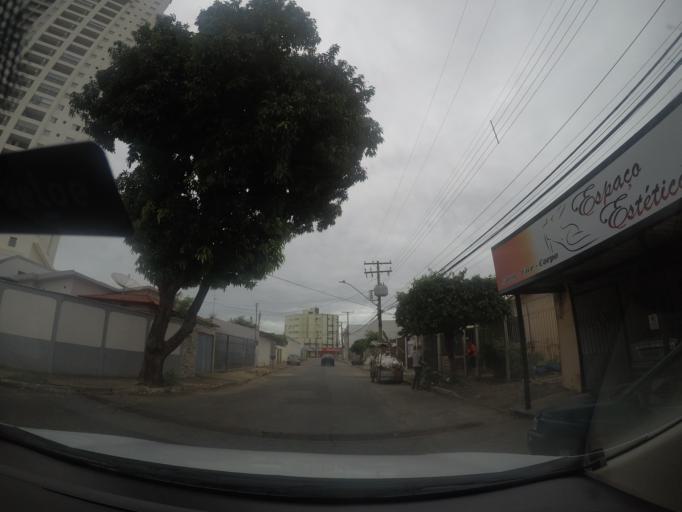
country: BR
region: Goias
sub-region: Goiania
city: Goiania
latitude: -16.6772
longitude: -49.2846
